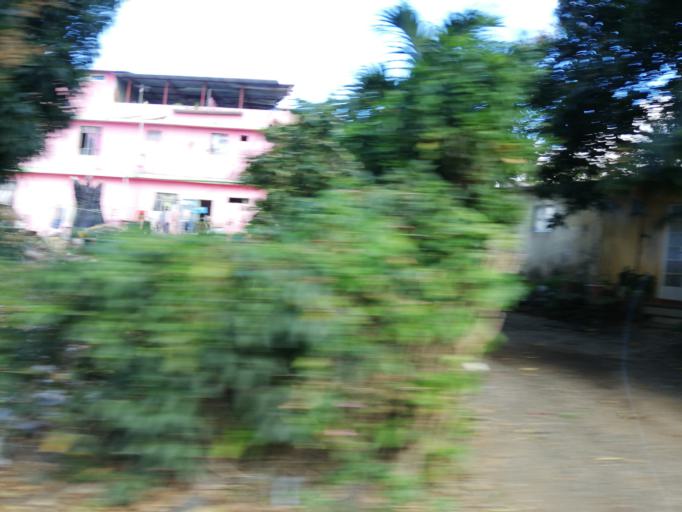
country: MU
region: Flacq
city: Bel Air Riviere Seche
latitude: -20.2627
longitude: 57.7418
